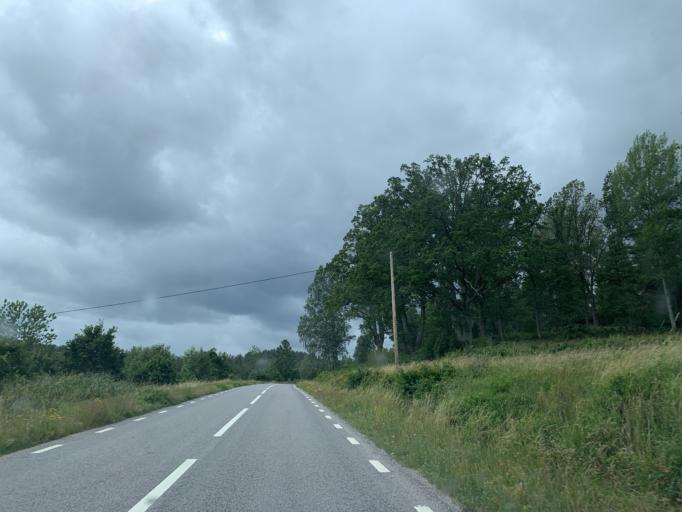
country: SE
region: Kalmar
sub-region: Vasterviks Kommun
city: Overum
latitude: 58.0231
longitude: 16.1255
